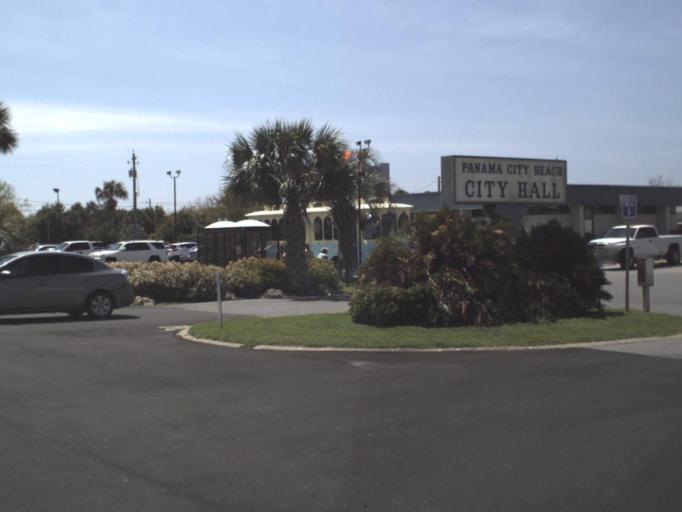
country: US
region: Florida
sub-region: Bay County
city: Laguna Beach
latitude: 30.2291
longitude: -85.8883
